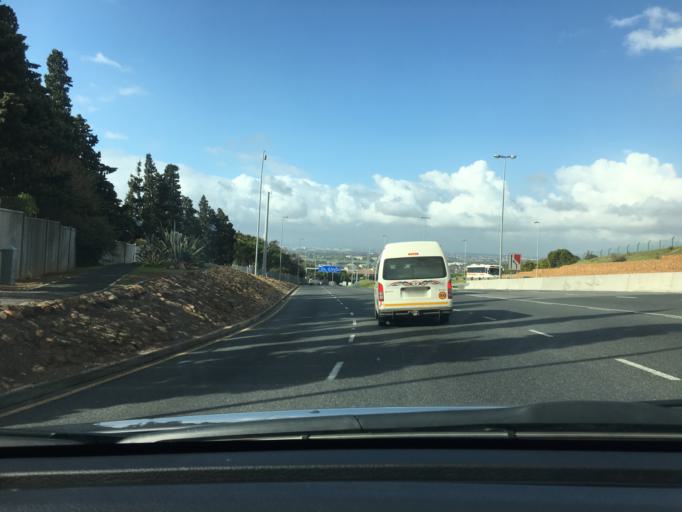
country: ZA
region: Western Cape
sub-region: City of Cape Town
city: Rosebank
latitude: -33.9432
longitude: 18.4597
